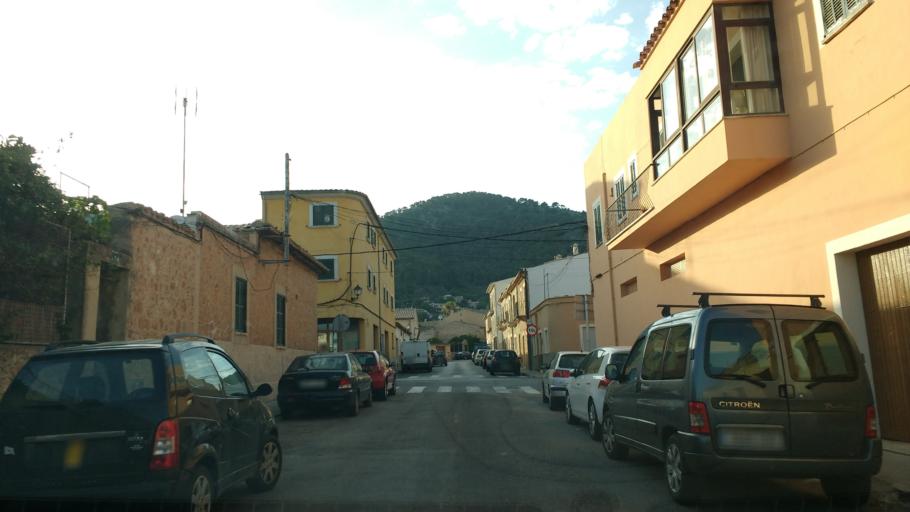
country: ES
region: Balearic Islands
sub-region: Illes Balears
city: Alaro
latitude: 39.7054
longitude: 2.7941
